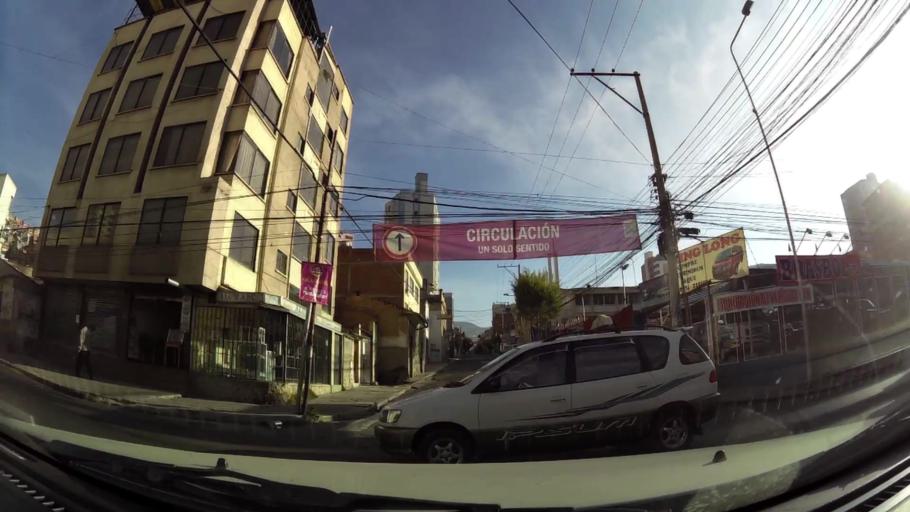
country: BO
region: La Paz
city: La Paz
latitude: -16.4971
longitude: -68.1231
